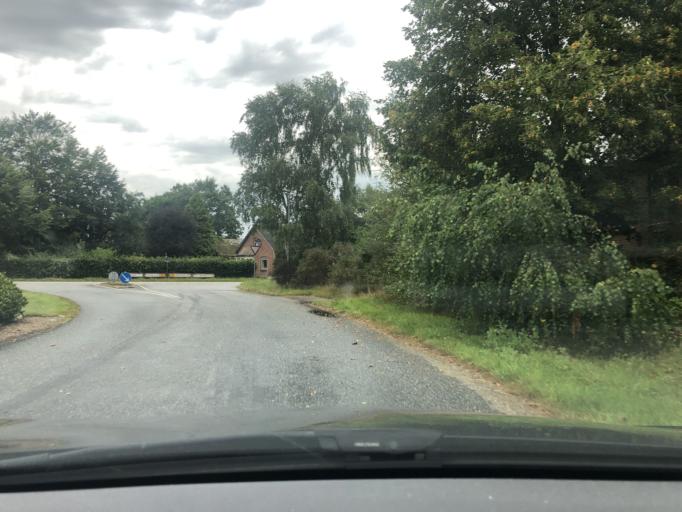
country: DK
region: South Denmark
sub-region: Varde Kommune
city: Olgod
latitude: 55.8182
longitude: 8.6819
